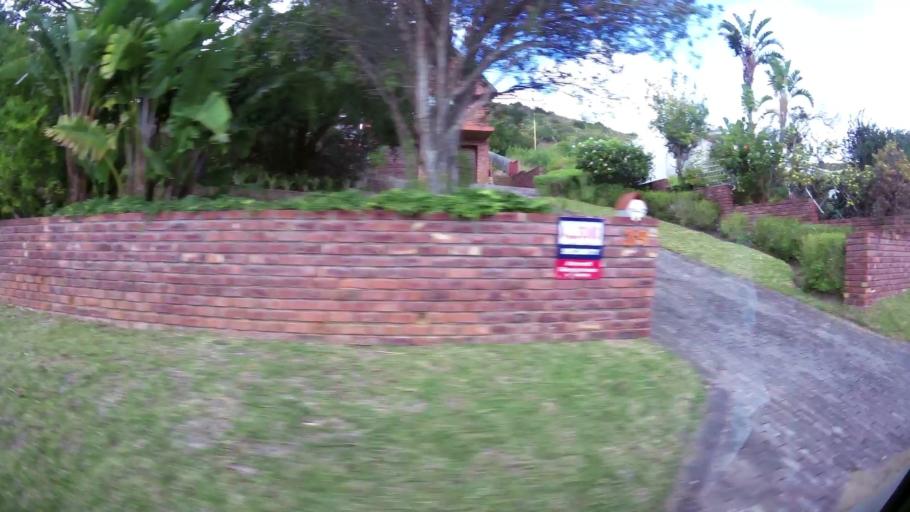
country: ZA
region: Western Cape
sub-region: Eden District Municipality
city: Knysna
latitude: -34.0652
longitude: 23.0813
